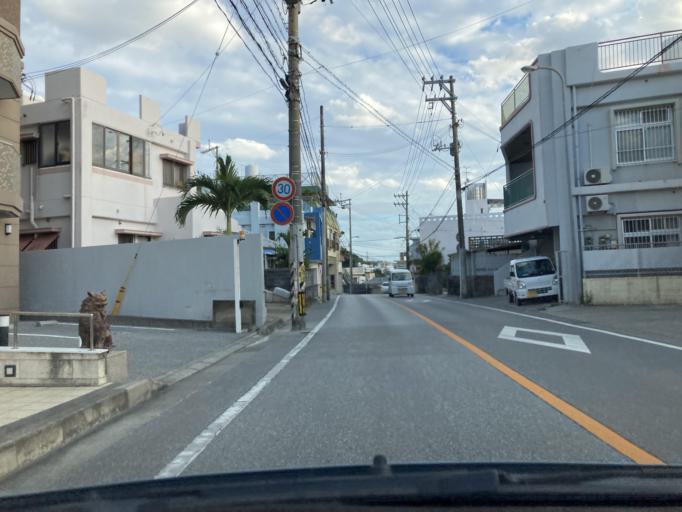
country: JP
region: Okinawa
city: Chatan
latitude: 26.3166
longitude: 127.7720
